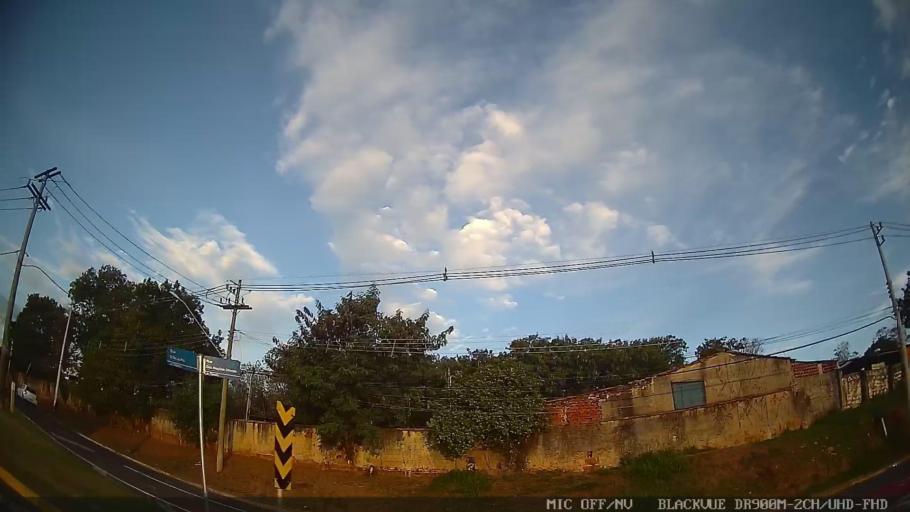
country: BR
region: Sao Paulo
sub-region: Salto
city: Salto
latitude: -23.1898
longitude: -47.2796
